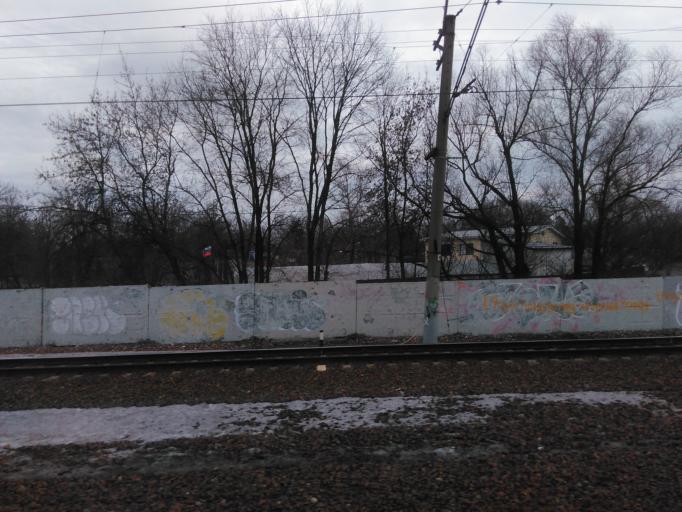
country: RU
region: Moskovskaya
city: Mamontovka
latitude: 56.0018
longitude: 37.8334
